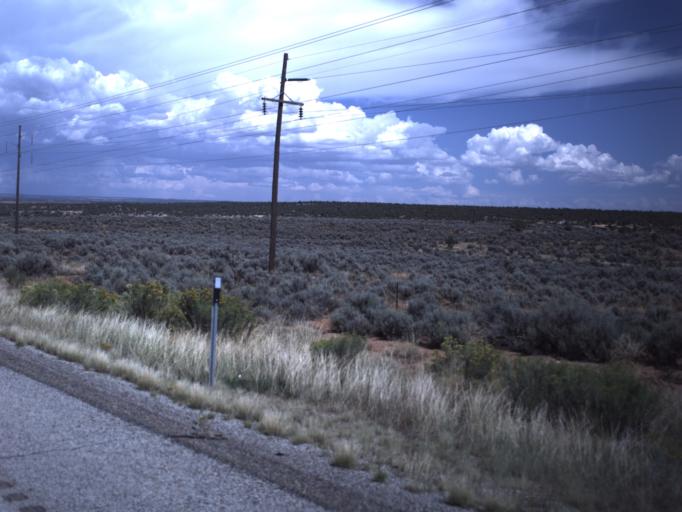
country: US
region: Utah
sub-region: San Juan County
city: Blanding
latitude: 37.5239
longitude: -109.4941
